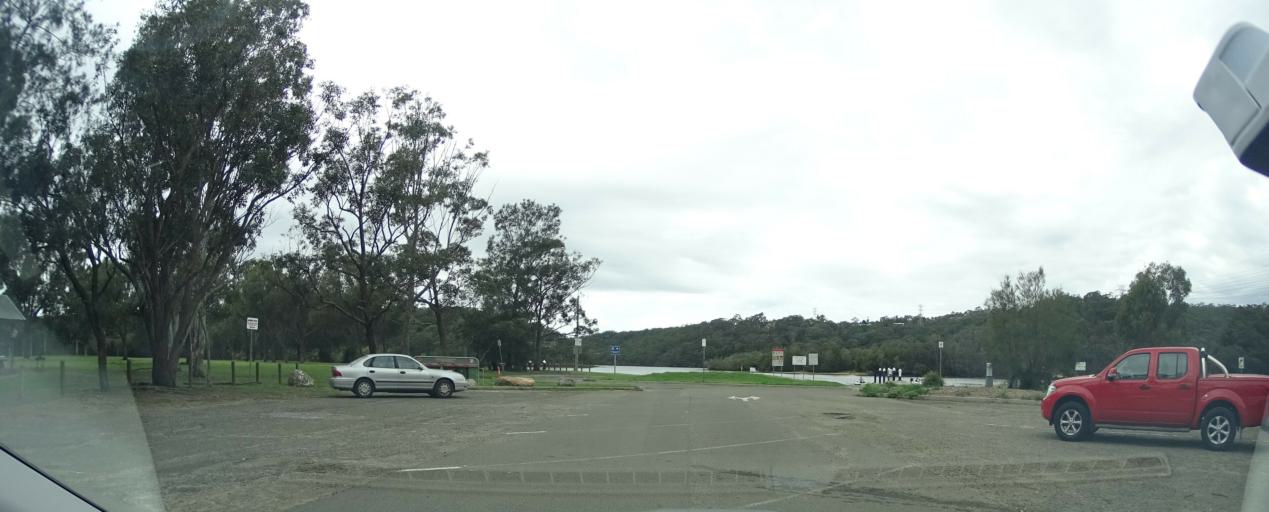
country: AU
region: New South Wales
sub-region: Bankstown
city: Padstow
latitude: -33.9755
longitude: 151.0190
